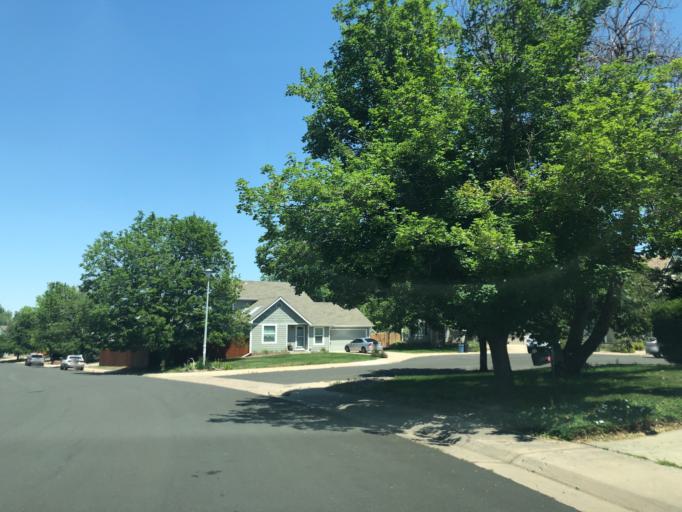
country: US
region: Colorado
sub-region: Arapahoe County
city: Dove Valley
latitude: 39.6246
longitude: -104.7779
